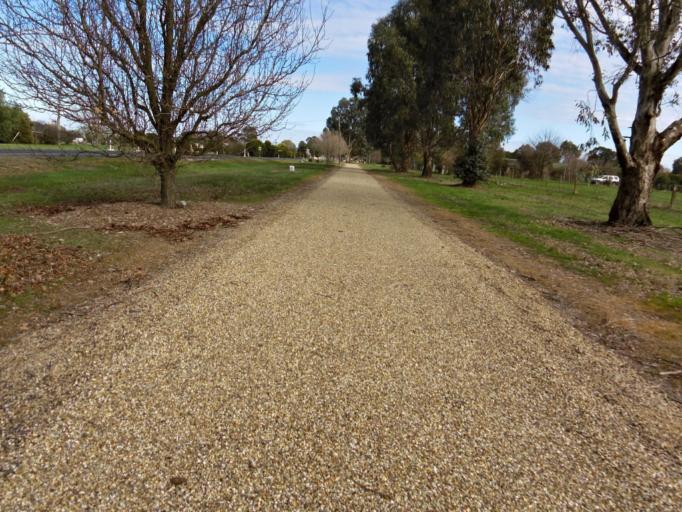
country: AU
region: Victoria
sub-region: Wangaratta
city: Wangaratta
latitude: -36.4501
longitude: 146.4371
